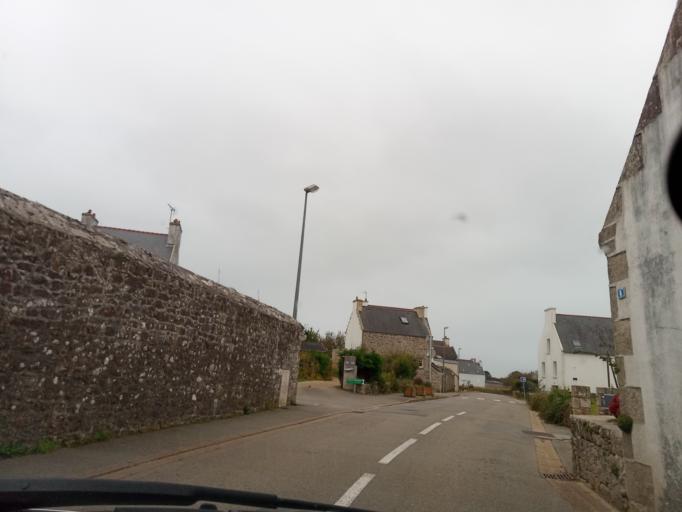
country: FR
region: Brittany
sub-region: Departement du Finistere
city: Esquibien
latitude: 48.0236
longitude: -4.5629
